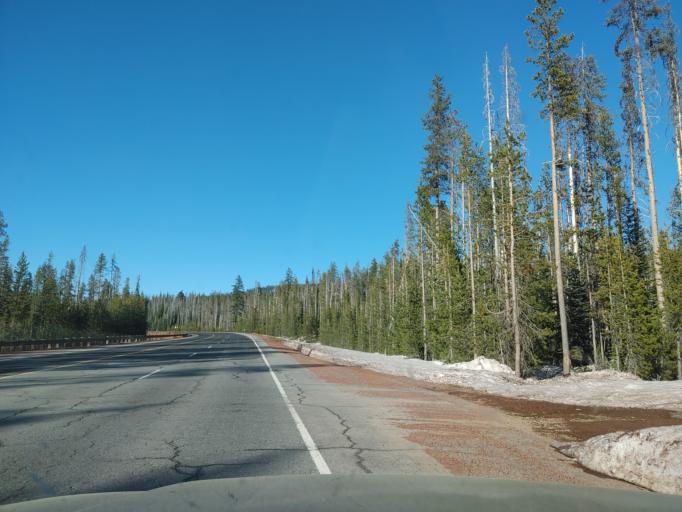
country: US
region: Oregon
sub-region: Lane County
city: Oakridge
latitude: 43.1306
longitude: -122.1283
